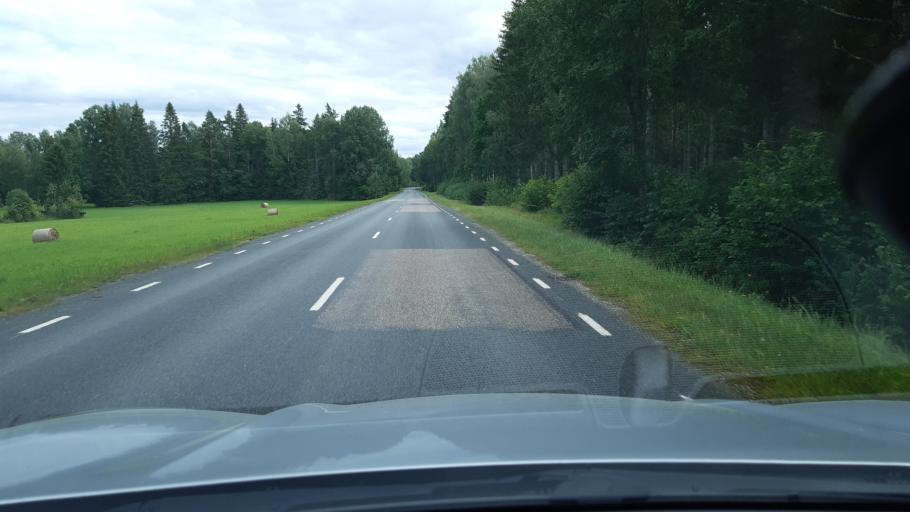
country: EE
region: Raplamaa
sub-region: Maerjamaa vald
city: Marjamaa
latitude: 59.0417
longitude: 24.5407
